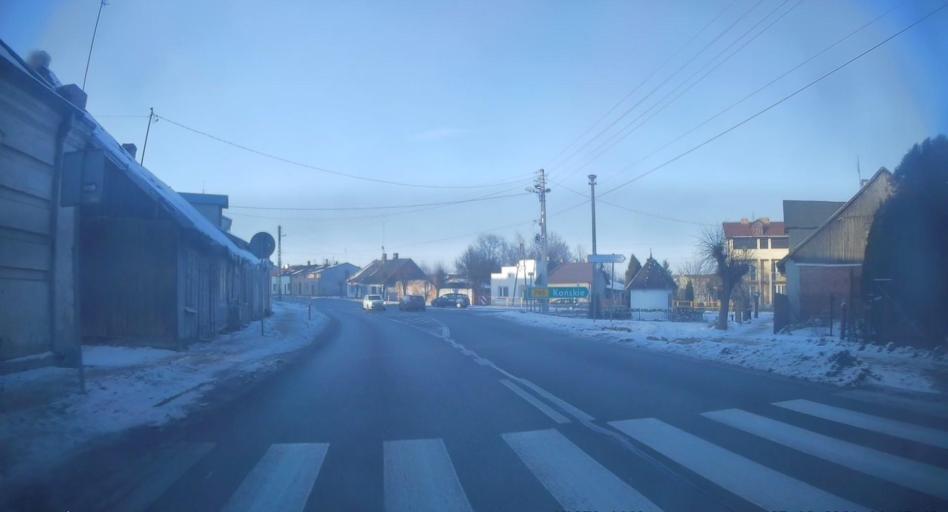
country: PL
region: Lodz Voivodeship
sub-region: Powiat opoczynski
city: Zarnow
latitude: 51.2455
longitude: 20.1747
